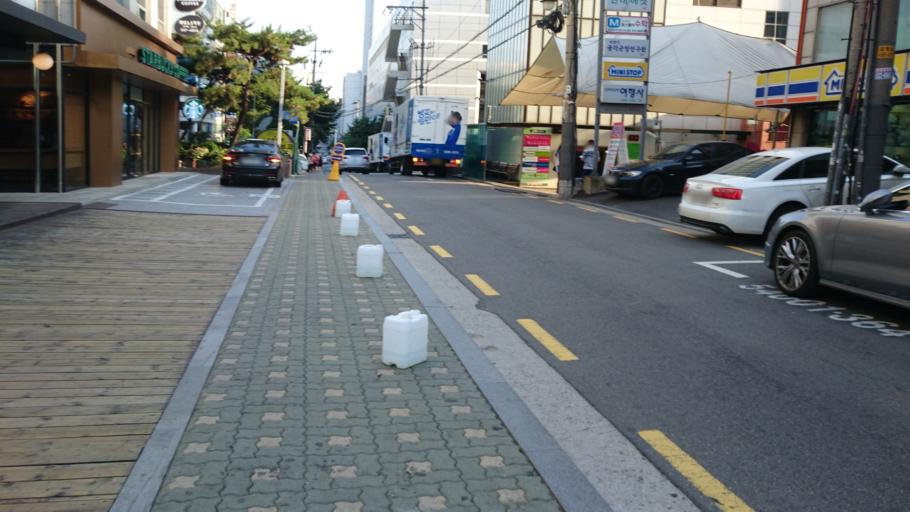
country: KR
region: Seoul
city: Seoul
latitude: 37.5264
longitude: 127.0293
